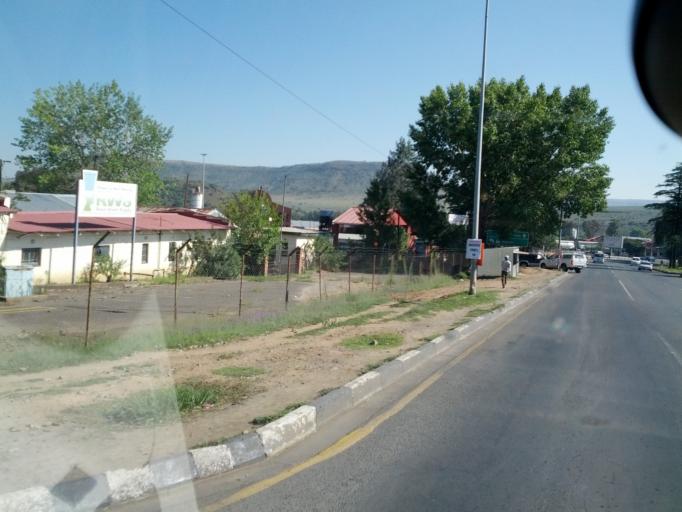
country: LS
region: Maseru
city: Maseru
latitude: -29.3009
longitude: 27.4687
